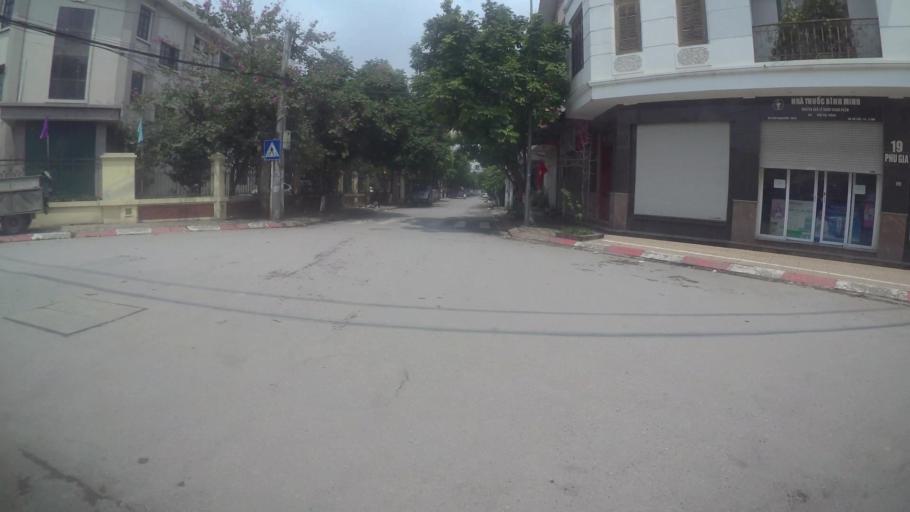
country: VN
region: Ha Noi
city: Tay Ho
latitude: 21.0881
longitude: 105.8089
